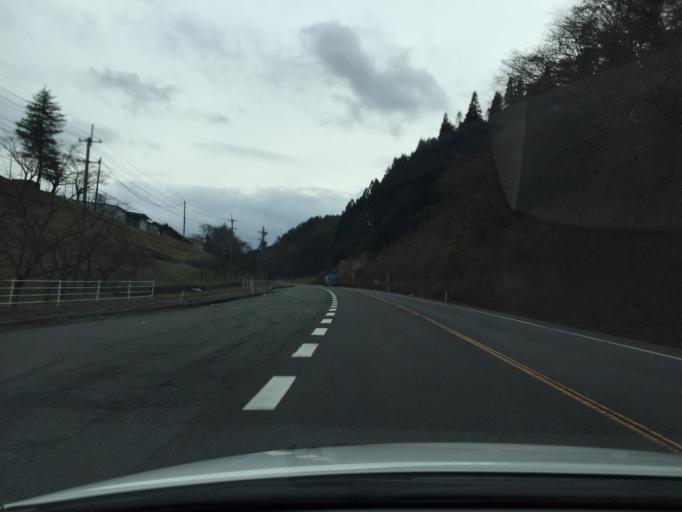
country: JP
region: Fukushima
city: Ishikawa
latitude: 37.1762
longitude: 140.6499
